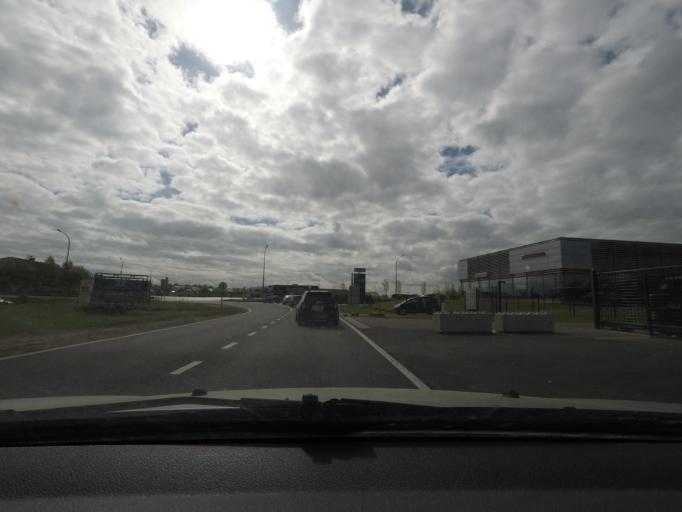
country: BE
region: Wallonia
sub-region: Province du Luxembourg
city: Habay-la-Vieille
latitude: 49.7041
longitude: 5.6225
